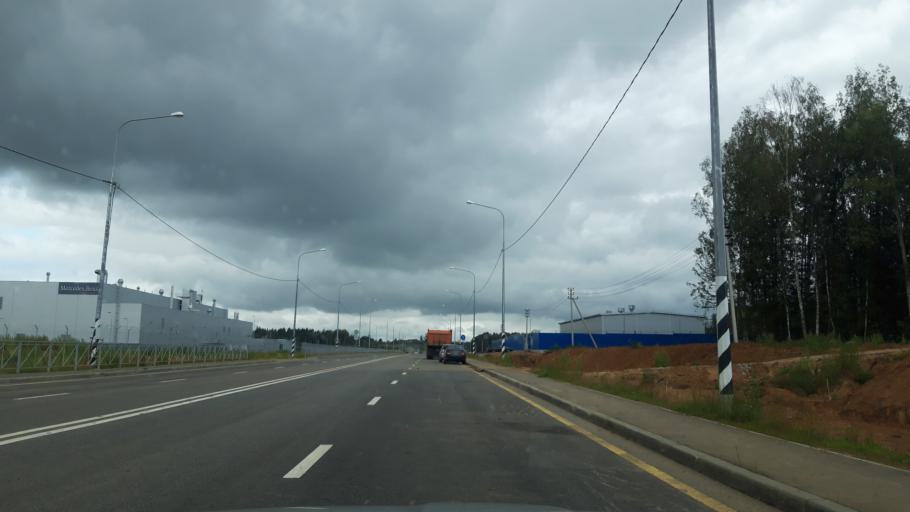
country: RU
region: Moskovskaya
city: Lozhki
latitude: 56.0823
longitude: 37.0883
